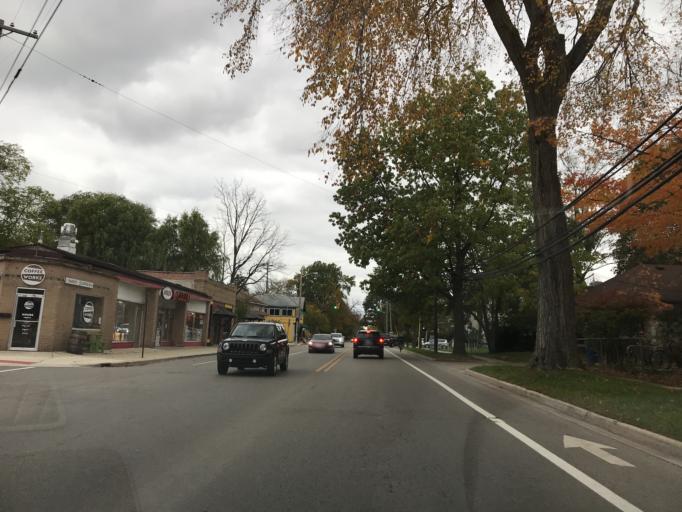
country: US
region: Michigan
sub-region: Washtenaw County
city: Ann Arbor
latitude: 42.2650
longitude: -83.7343
